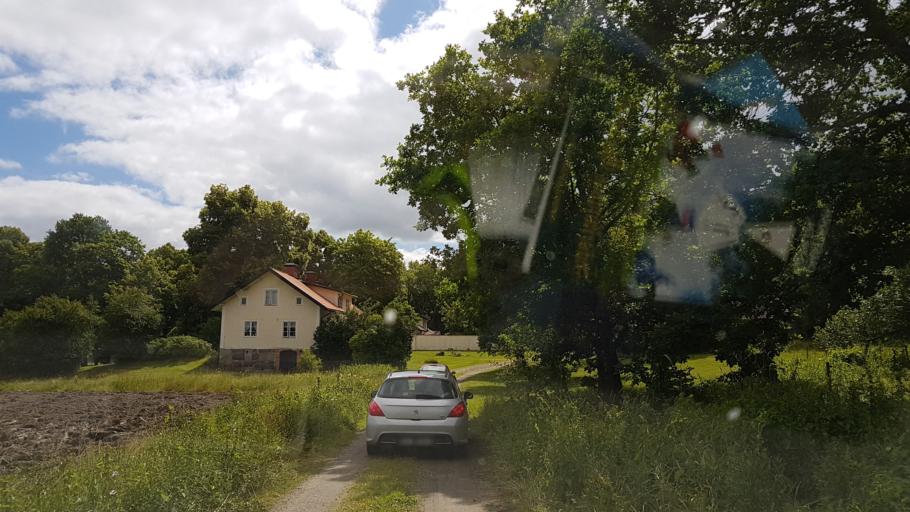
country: SE
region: OEstergoetland
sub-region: Valdemarsviks Kommun
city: Gusum
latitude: 58.4276
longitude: 16.5872
